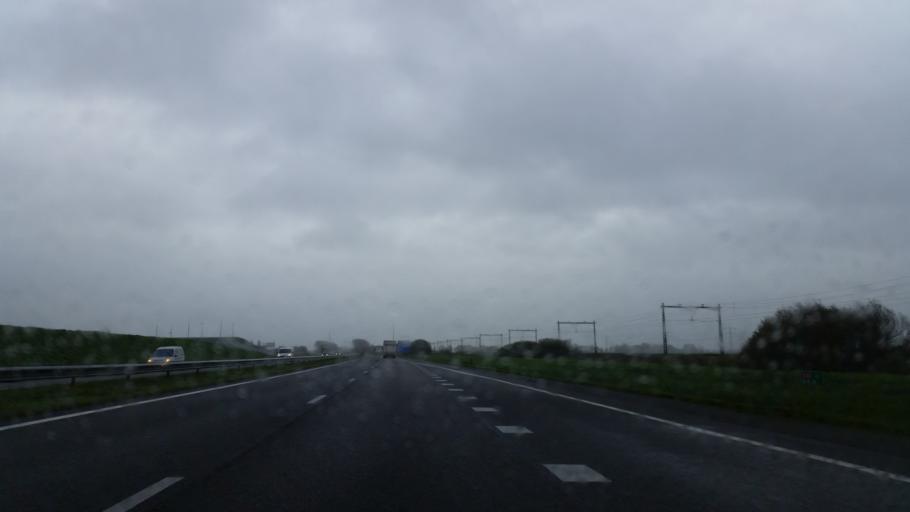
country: NL
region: Friesland
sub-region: Gemeente Boarnsterhim
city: Grou
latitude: 53.1044
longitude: 5.8160
